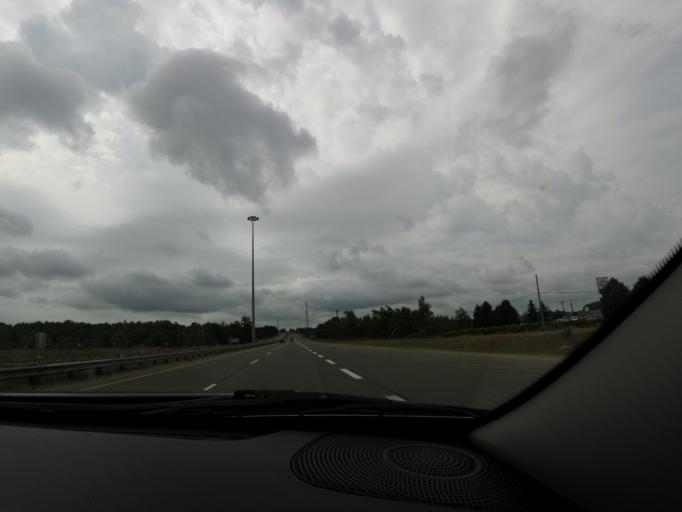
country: CA
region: Ontario
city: Orillia
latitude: 44.6092
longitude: -79.4457
